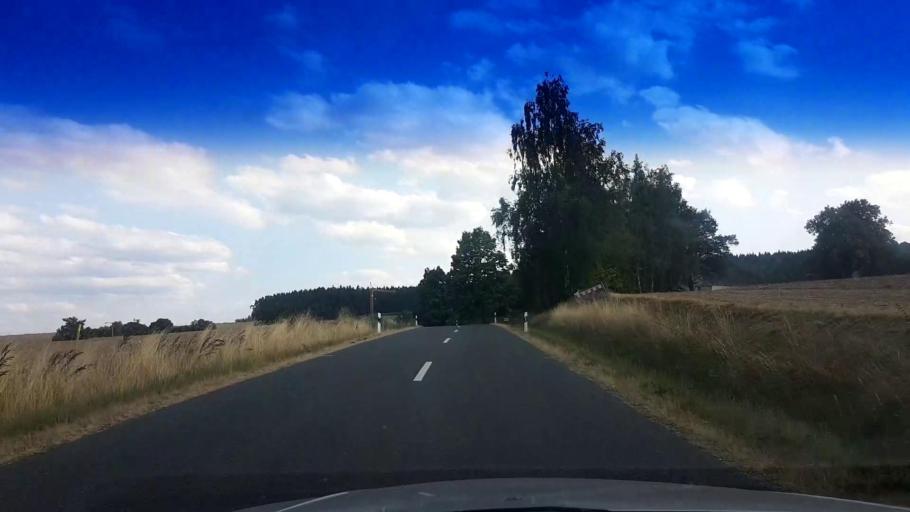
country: DE
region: Bavaria
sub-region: Upper Palatinate
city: Waldsassen
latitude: 50.0183
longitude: 12.3584
